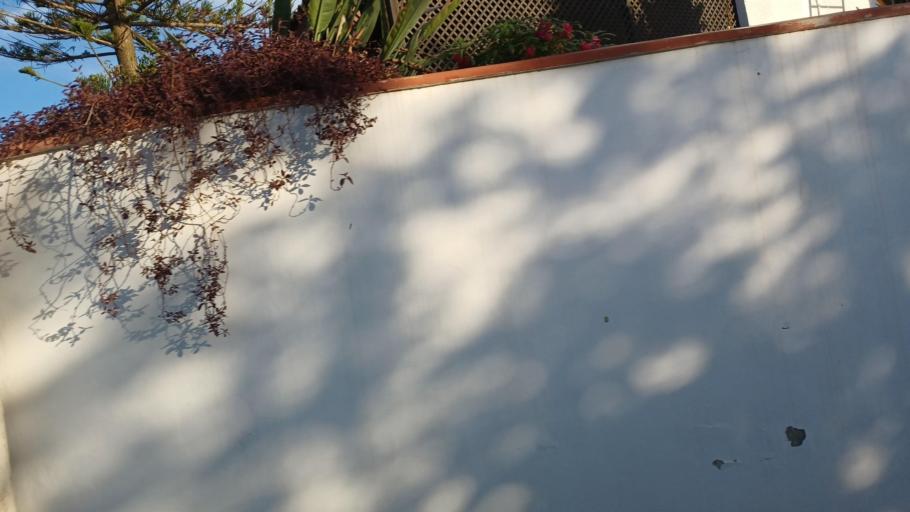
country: CY
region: Larnaka
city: Mosfiloti
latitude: 34.9264
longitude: 33.4335
